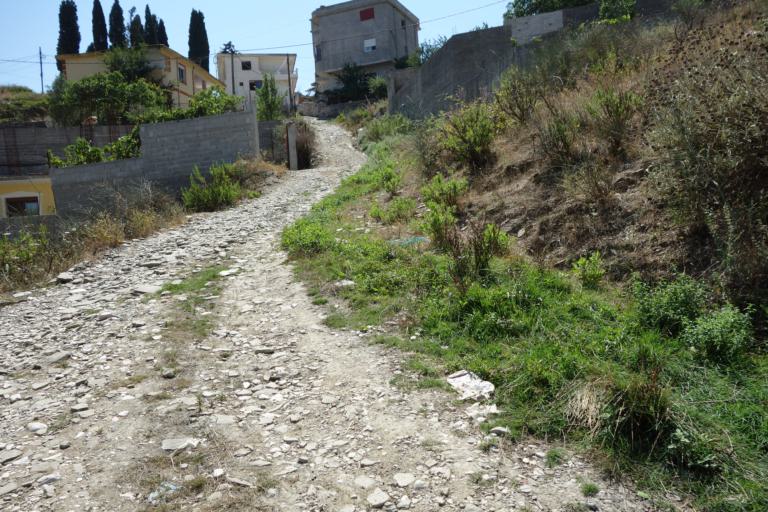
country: AL
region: Gjirokaster
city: Gjirokaster
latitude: 40.0835
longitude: 20.1341
